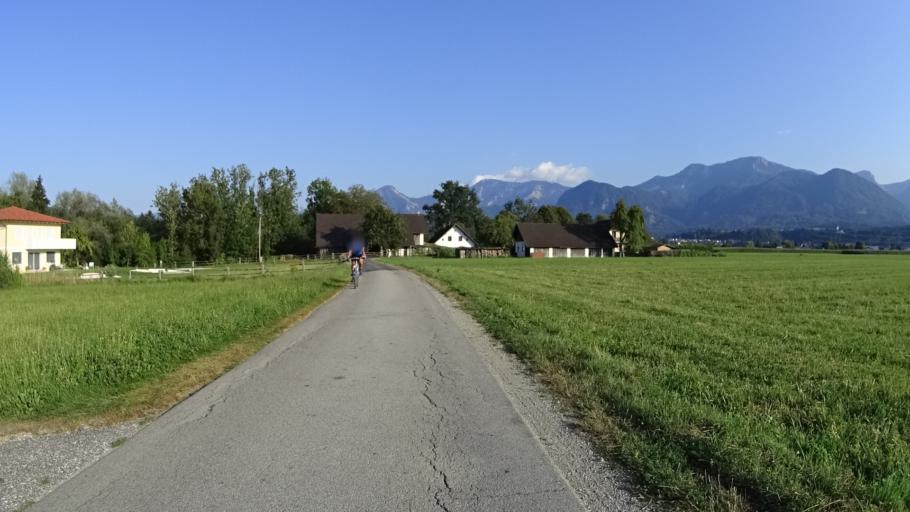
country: AT
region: Carinthia
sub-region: Politischer Bezirk Villach Land
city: Sankt Jakob
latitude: 46.5656
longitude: 14.0574
